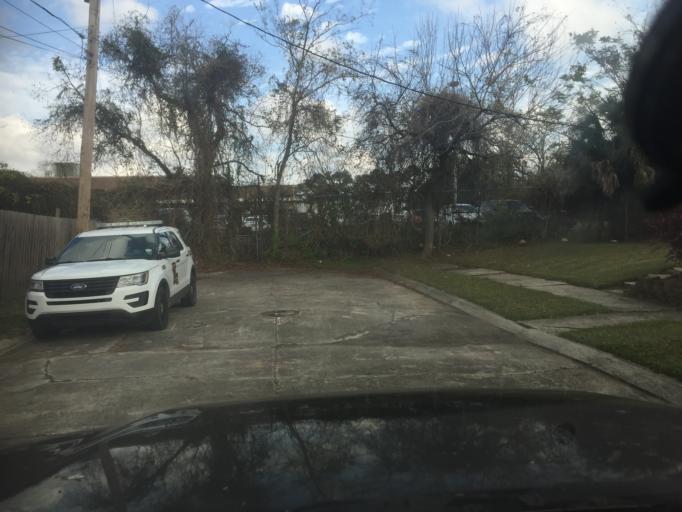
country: US
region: Louisiana
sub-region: Orleans Parish
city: New Orleans
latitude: 29.9906
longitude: -90.0787
